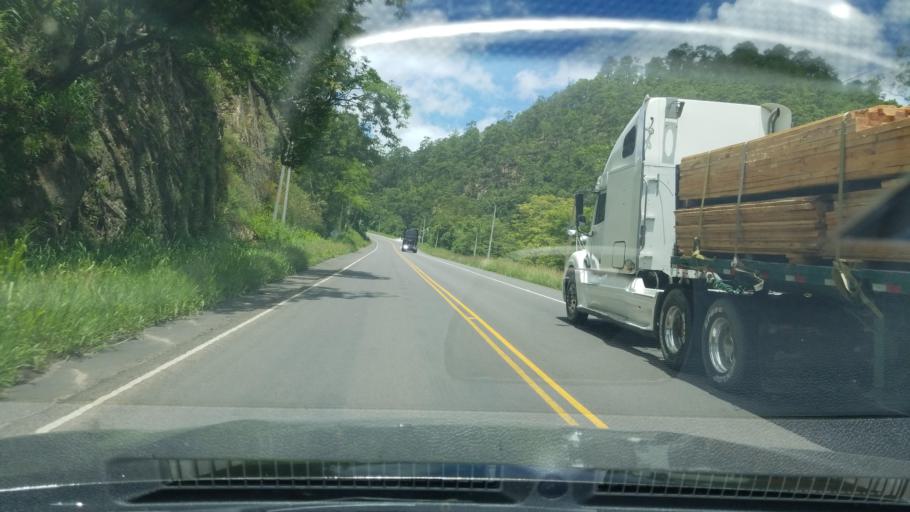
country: HN
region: Francisco Morazan
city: Talanga
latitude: 14.3907
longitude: -87.1325
